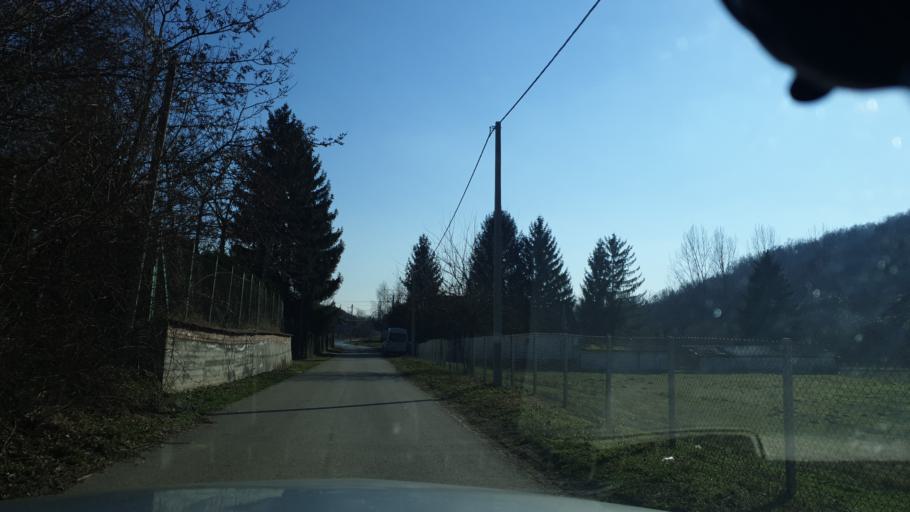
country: RS
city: Vrdnik
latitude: 45.1143
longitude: 19.7671
